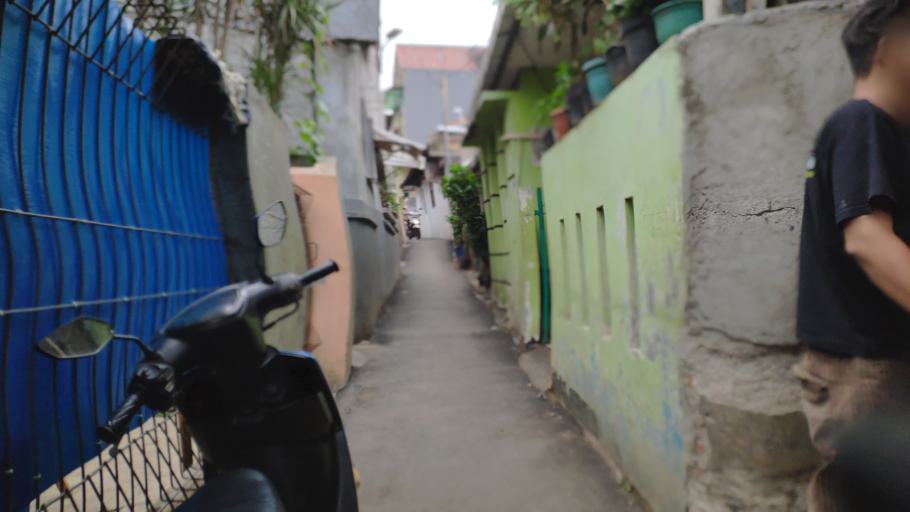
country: ID
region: West Java
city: Depok
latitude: -6.3118
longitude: 106.8344
